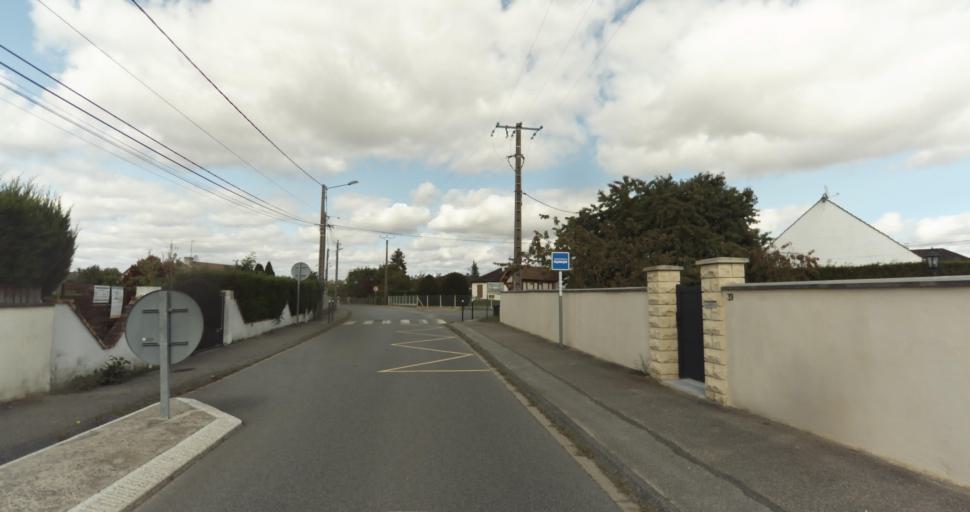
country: FR
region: Haute-Normandie
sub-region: Departement de l'Eure
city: La Couture-Boussey
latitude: 48.8919
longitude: 1.4047
